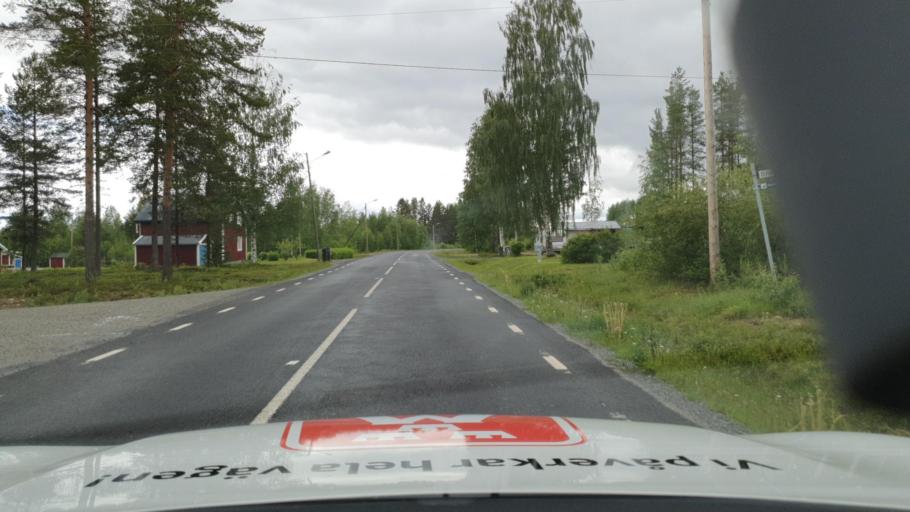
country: SE
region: Vaesterbotten
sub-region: Dorotea Kommun
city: Dorotea
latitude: 64.2170
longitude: 16.5472
